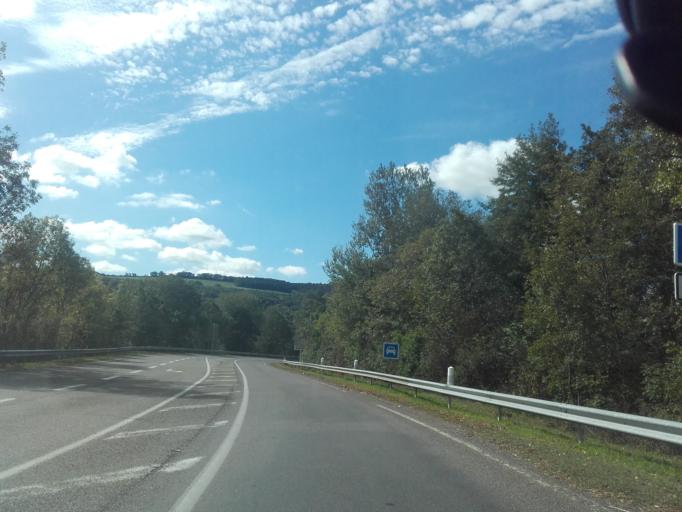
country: FR
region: Bourgogne
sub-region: Departement de Saone-et-Loire
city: Prisse
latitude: 46.3328
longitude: 4.7361
